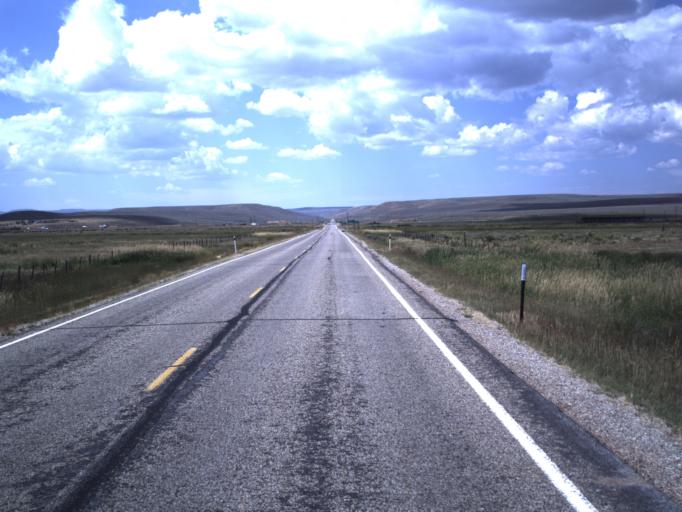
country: US
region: Utah
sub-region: Rich County
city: Randolph
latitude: 41.7737
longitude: -111.1096
